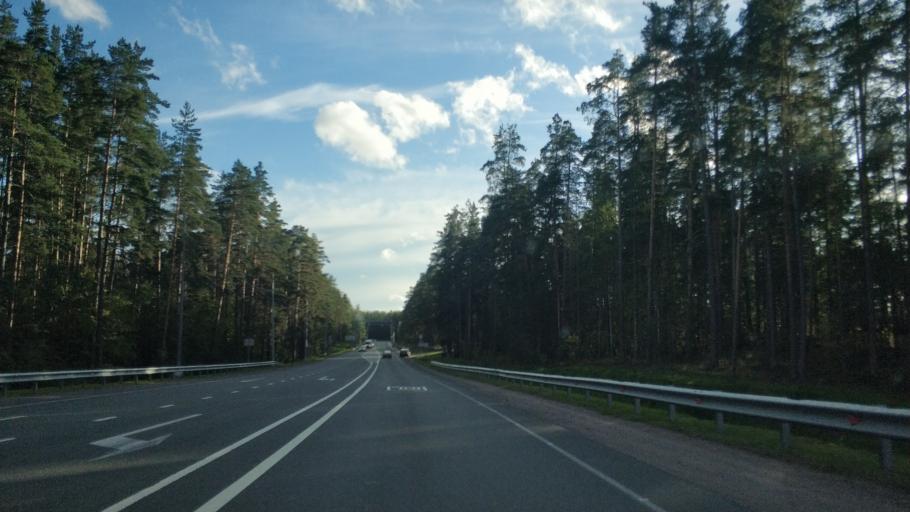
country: RU
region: Leningrad
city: Sapernoye
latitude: 60.7117
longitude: 29.9750
